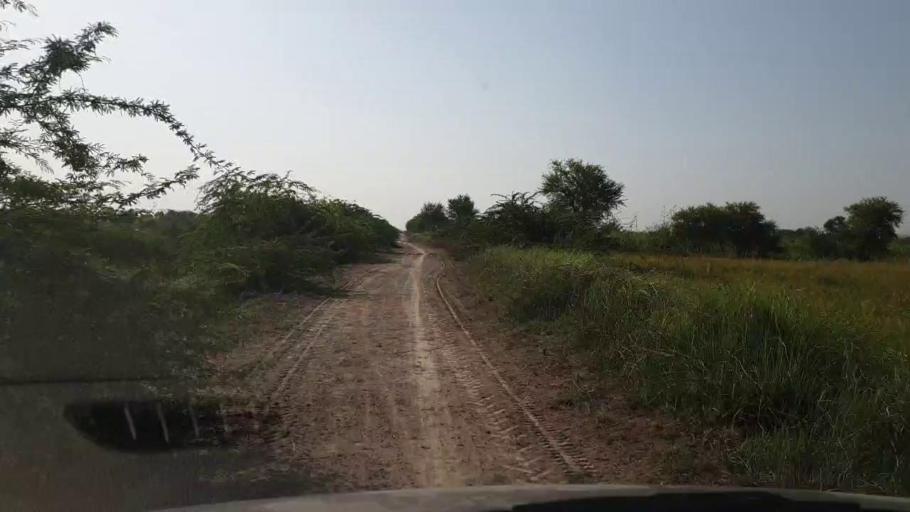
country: PK
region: Sindh
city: Kadhan
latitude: 24.6004
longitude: 69.0748
